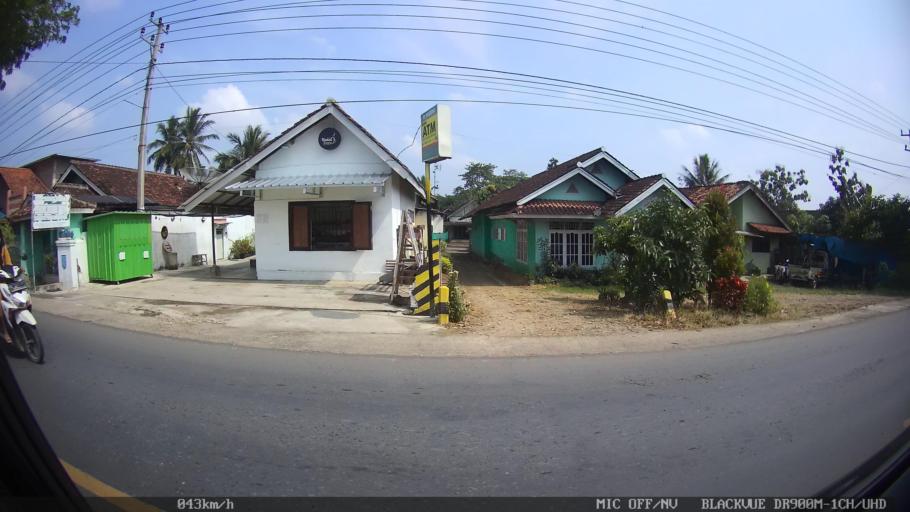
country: ID
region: Lampung
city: Gadingrejo
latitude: -5.3721
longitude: 105.0468
